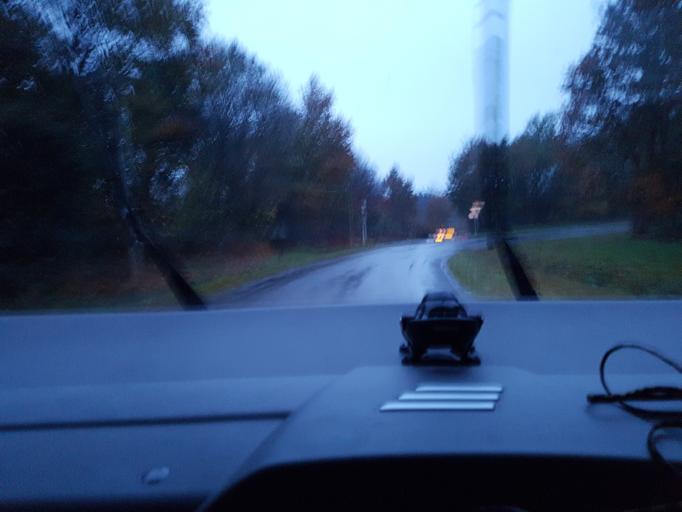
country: FR
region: Brittany
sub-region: Departement d'Ille-et-Vilaine
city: Montreuil-sous-Perouse
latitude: 48.1831
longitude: -1.2920
